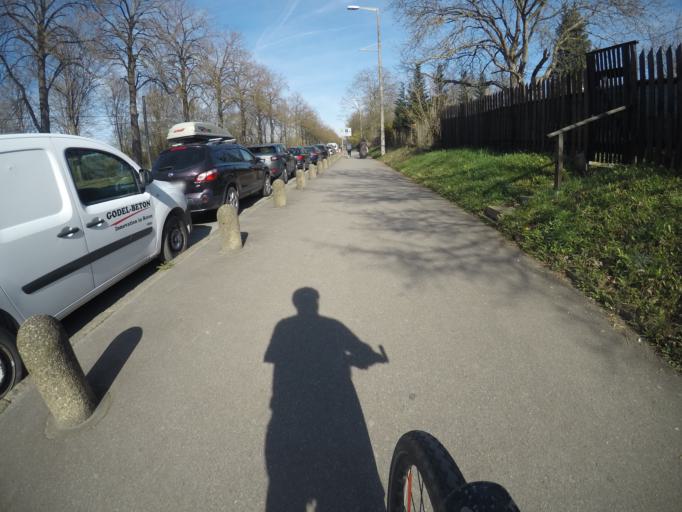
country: DE
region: Baden-Wuerttemberg
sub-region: Regierungsbezirk Stuttgart
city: Stuttgart Muehlhausen
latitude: 48.8302
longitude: 9.2132
